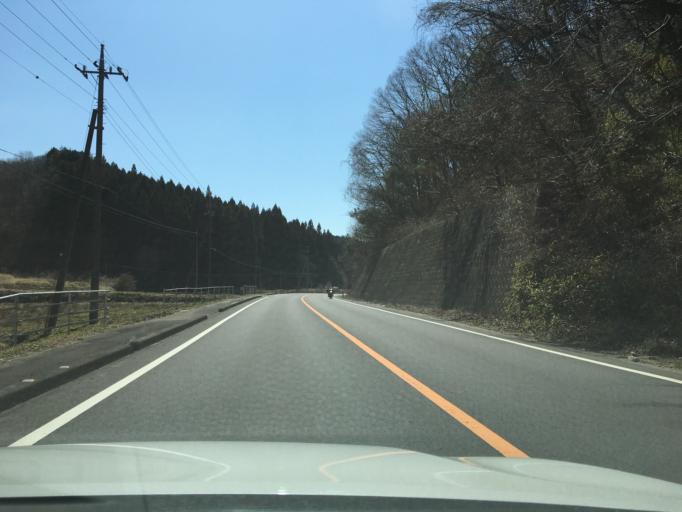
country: JP
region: Tochigi
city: Kuroiso
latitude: 37.0604
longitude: 140.1792
